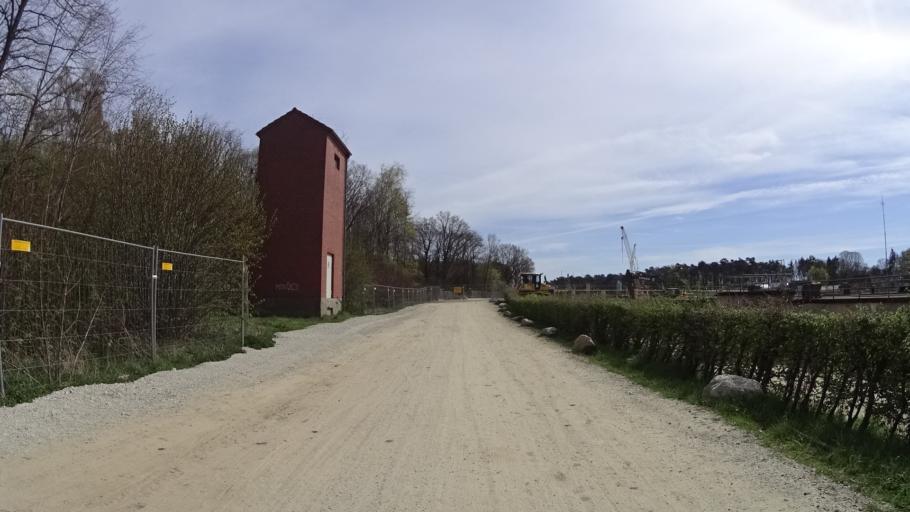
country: DE
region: Lower Saxony
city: Lingen
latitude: 52.4583
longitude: 7.3289
